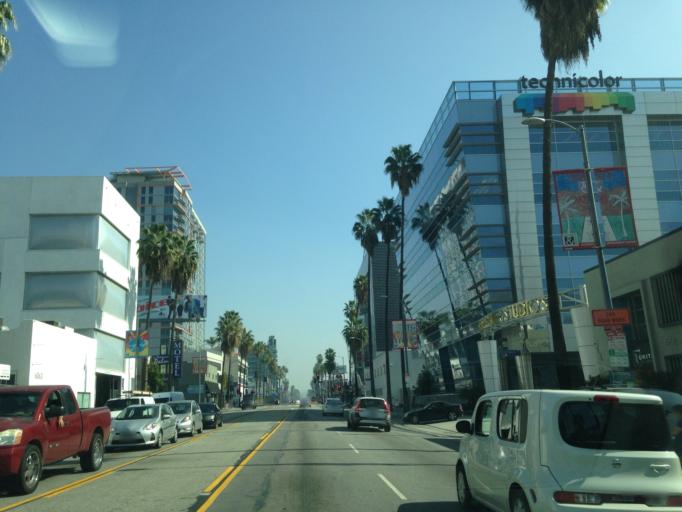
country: US
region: California
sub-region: Los Angeles County
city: Hollywood
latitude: 34.0980
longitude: -118.3216
